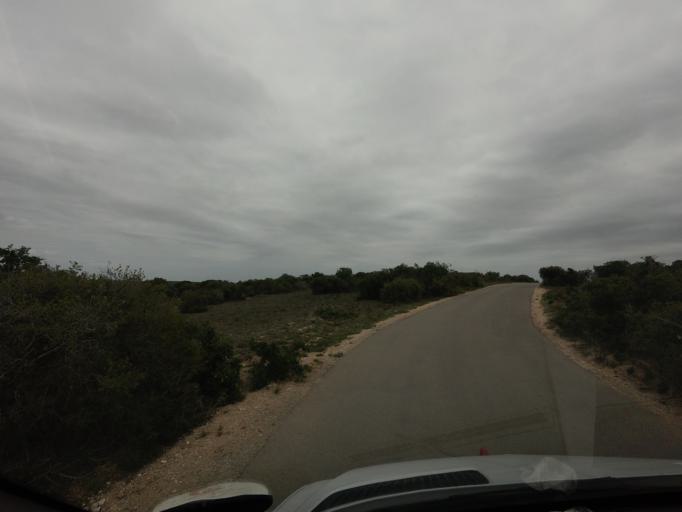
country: ZA
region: Eastern Cape
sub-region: Cacadu District Municipality
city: Kirkwood
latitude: -33.4631
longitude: 25.7841
